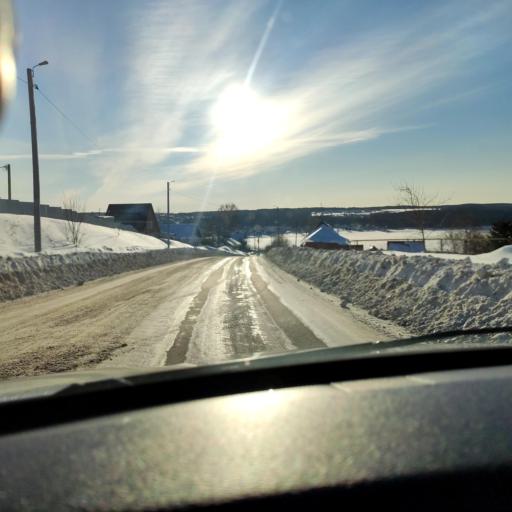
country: RU
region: Perm
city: Polazna
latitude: 58.3112
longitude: 56.4279
